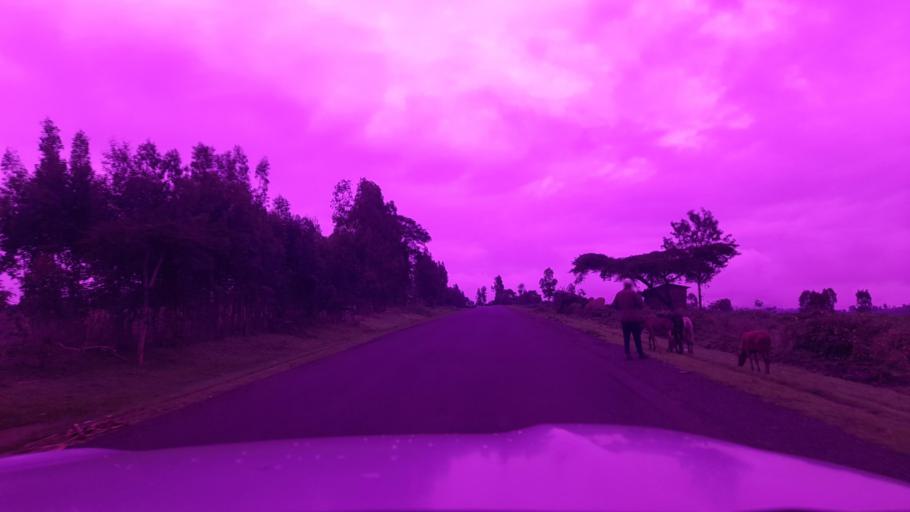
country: ET
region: Oromiya
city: Waliso
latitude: 8.2743
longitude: 37.6767
